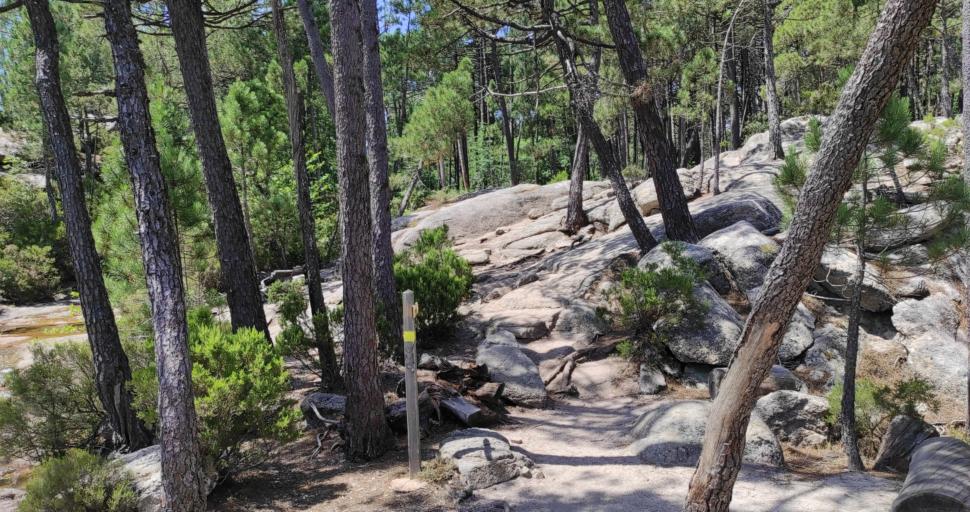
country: FR
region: Corsica
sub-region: Departement de la Corse-du-Sud
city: Zonza
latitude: 41.6862
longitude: 9.2012
